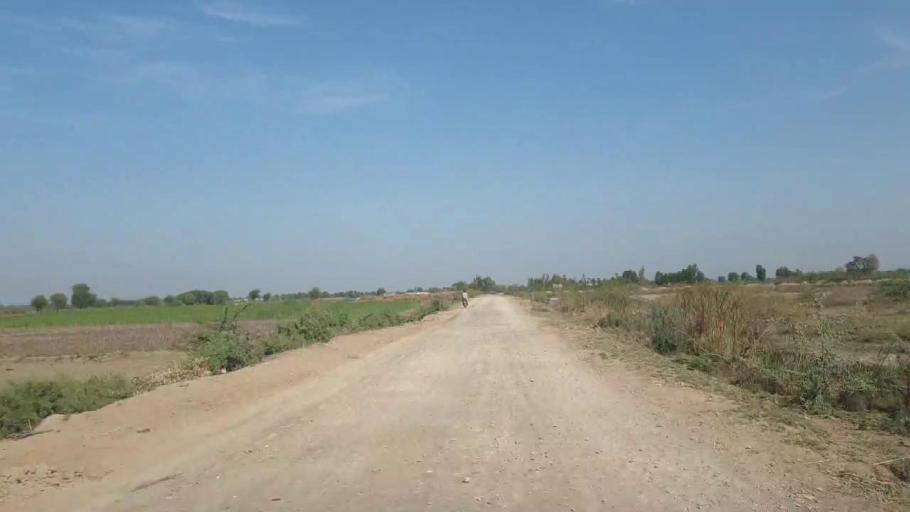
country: PK
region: Sindh
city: Samaro
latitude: 25.3793
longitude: 69.2589
